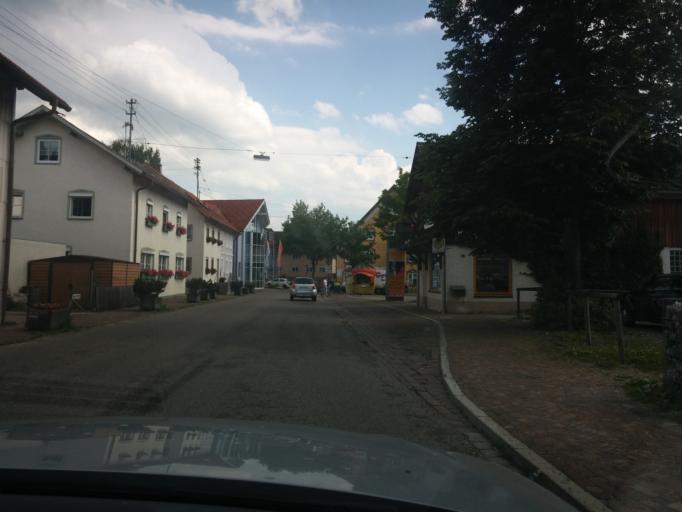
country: DE
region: Bavaria
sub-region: Swabia
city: Altusried
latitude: 47.8056
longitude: 10.2140
